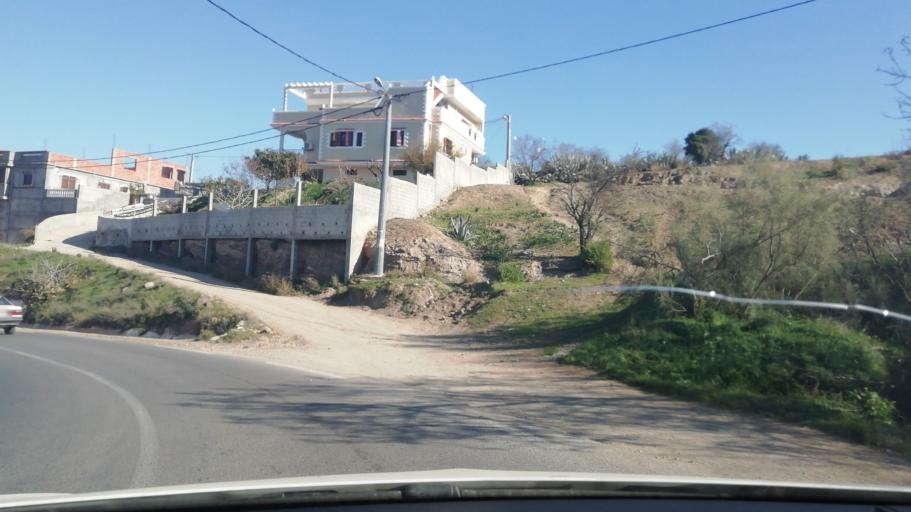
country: DZ
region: Tlemcen
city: Nedroma
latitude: 35.0673
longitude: -1.8833
